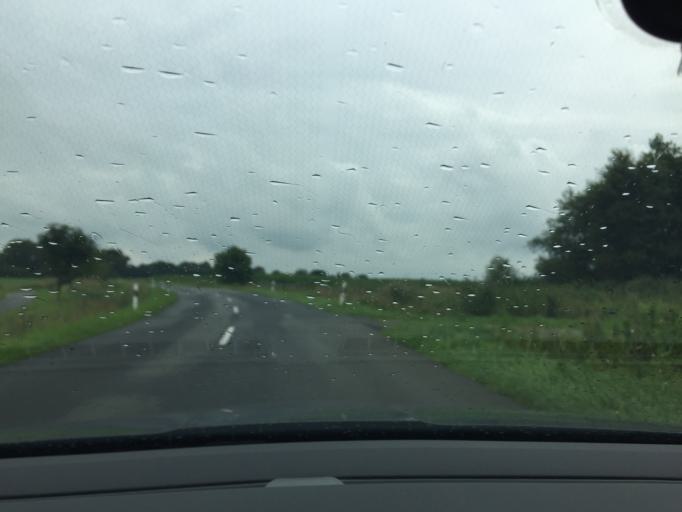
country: DE
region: Lower Saxony
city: Jemgum
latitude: 53.3711
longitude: 7.4154
